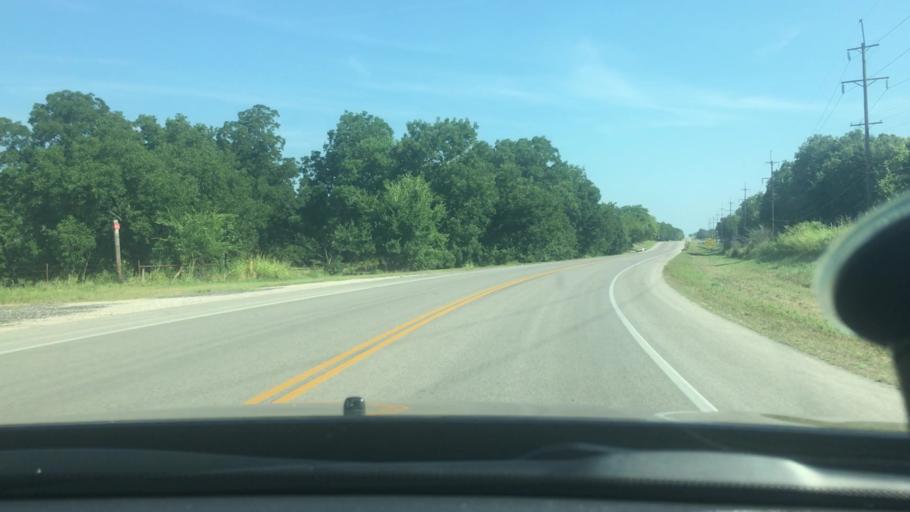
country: US
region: Oklahoma
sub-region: Garvin County
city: Pauls Valley
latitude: 34.6852
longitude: -97.2128
